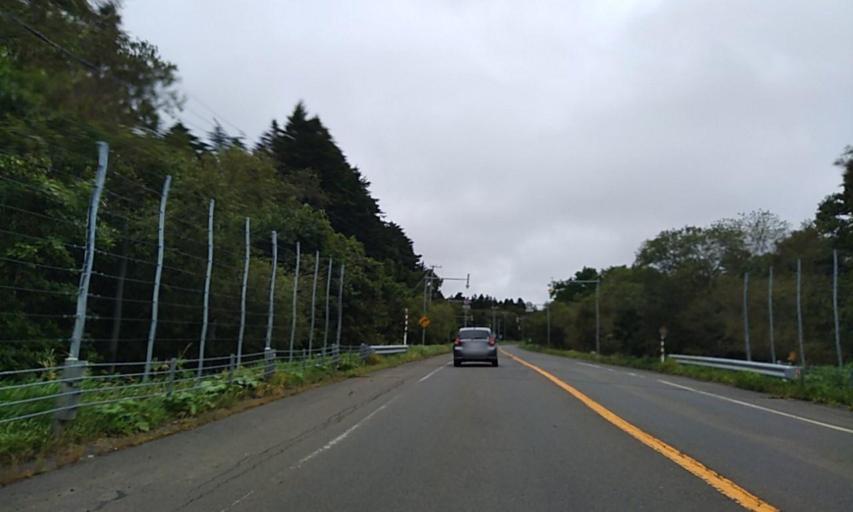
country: JP
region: Hokkaido
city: Nemuro
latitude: 43.2602
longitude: 145.4102
